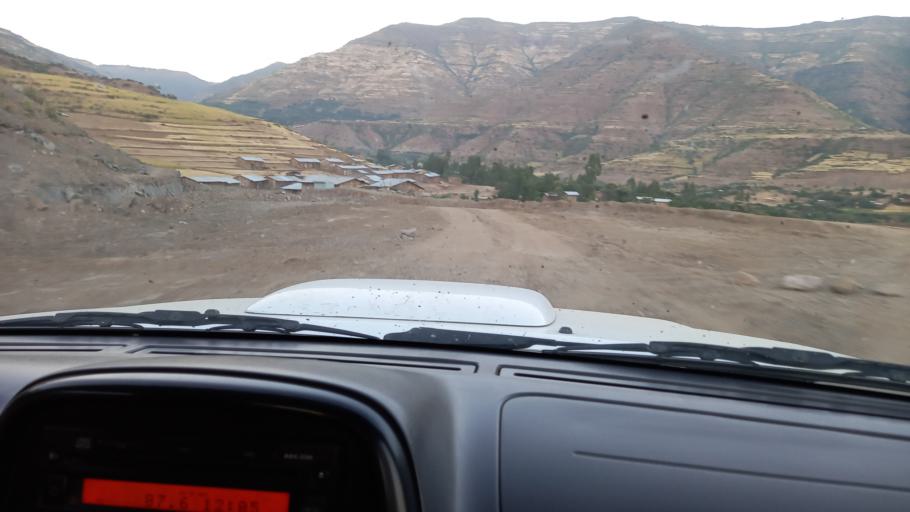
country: ET
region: Amhara
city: Debark'
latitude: 13.0360
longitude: 38.0431
